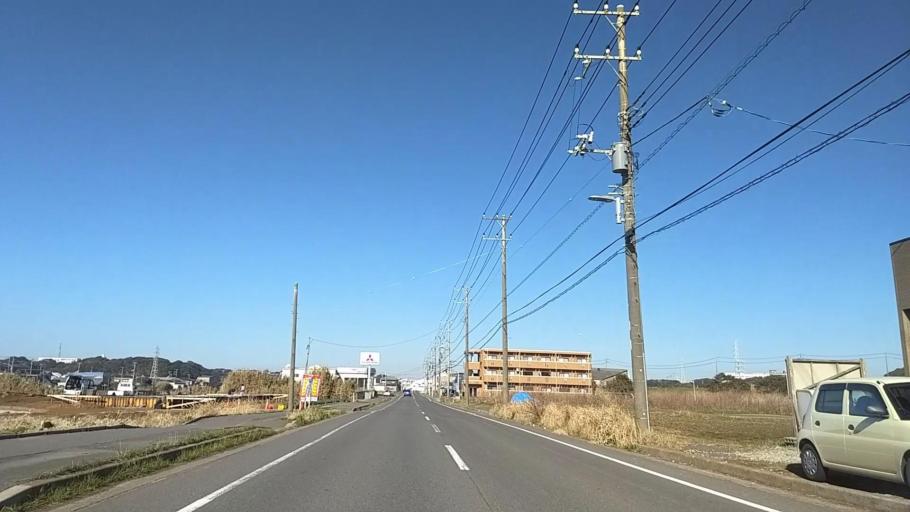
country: JP
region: Chiba
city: Hasaki
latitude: 35.7155
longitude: 140.8394
